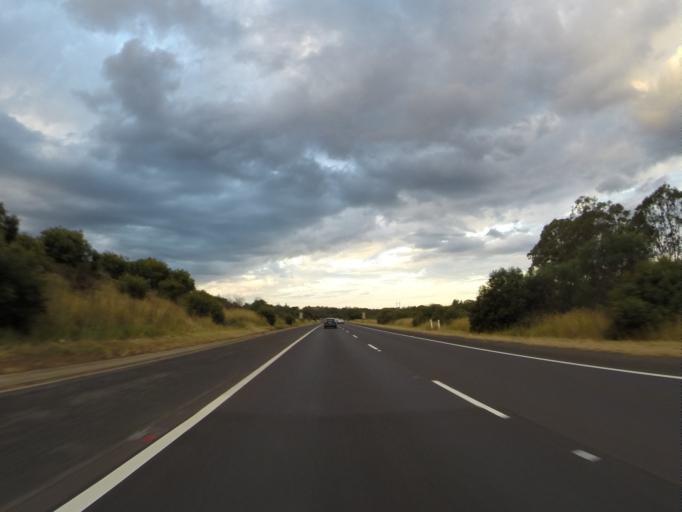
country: AU
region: New South Wales
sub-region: Wollondilly
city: Douglas Park
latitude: -34.1814
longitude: 150.7230
